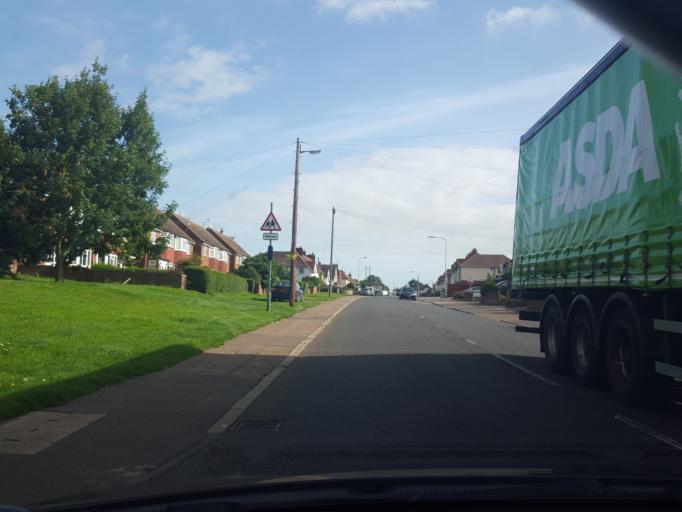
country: GB
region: England
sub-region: Essex
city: Dovercourt
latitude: 51.9367
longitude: 1.2588
